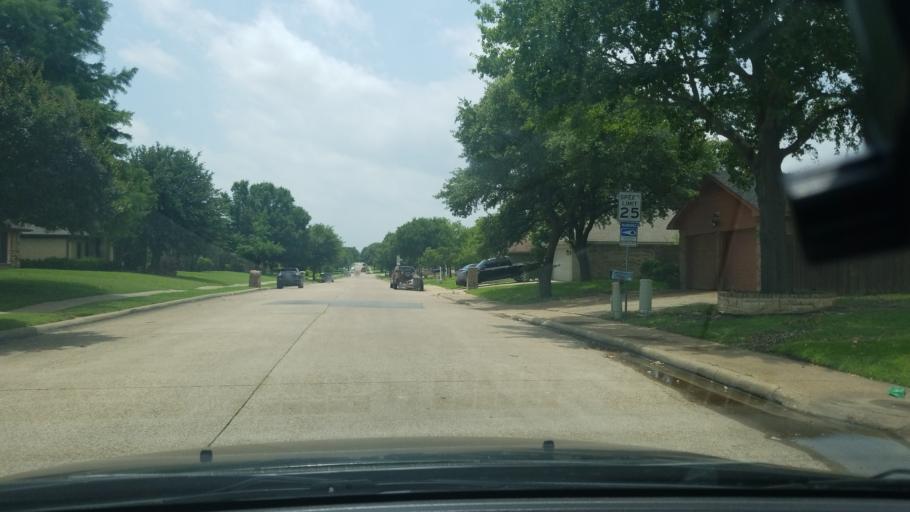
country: US
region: Texas
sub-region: Dallas County
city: Mesquite
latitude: 32.8049
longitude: -96.6155
